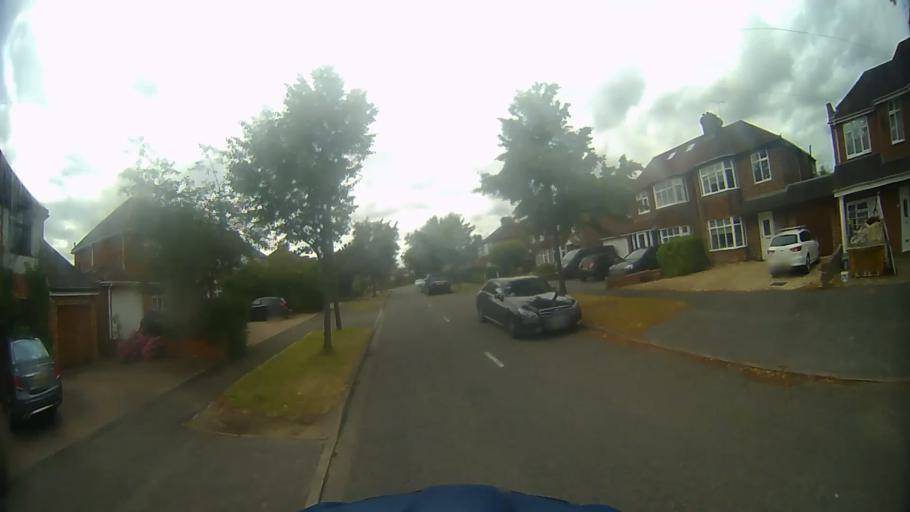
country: GB
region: England
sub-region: Wokingham
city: Earley
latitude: 51.4549
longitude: -0.9335
